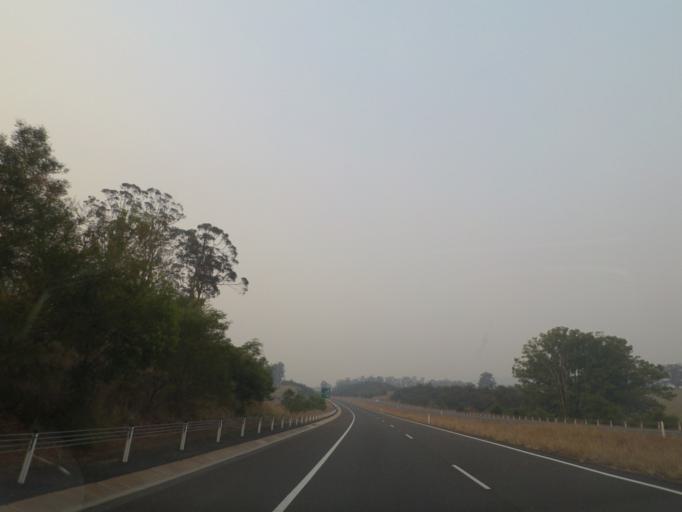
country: AU
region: New South Wales
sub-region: Nambucca Shire
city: Macksville
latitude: -30.7683
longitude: 152.9026
